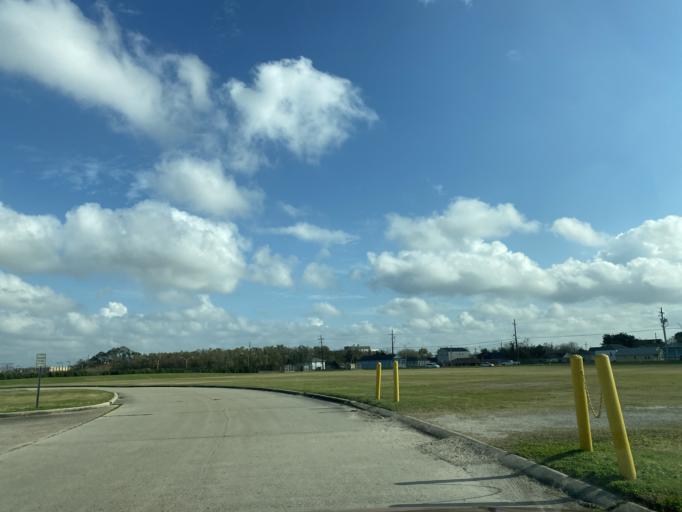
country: US
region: Louisiana
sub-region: Orleans Parish
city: New Orleans
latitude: 30.0282
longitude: -90.0507
